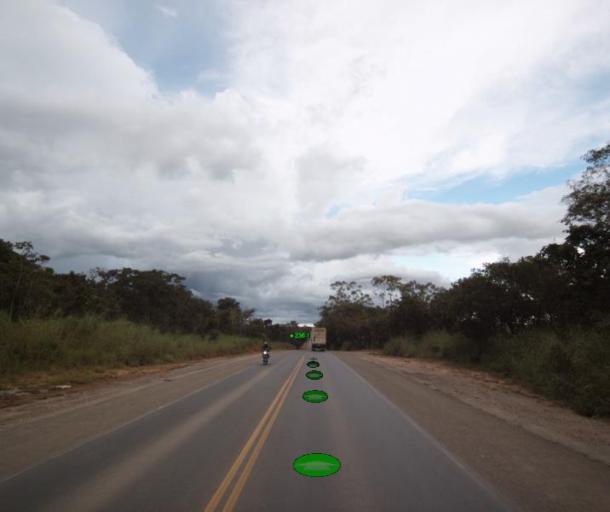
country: BR
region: Goias
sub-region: Itapaci
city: Itapaci
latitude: -14.8139
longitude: -49.2934
